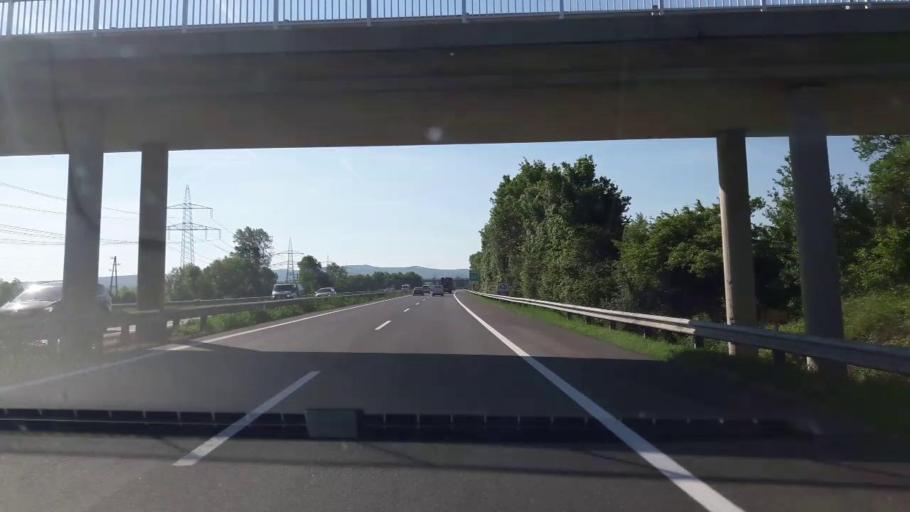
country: AT
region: Lower Austria
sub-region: Politischer Bezirk Baden
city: Ebreichsdorf
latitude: 47.9247
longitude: 16.3967
